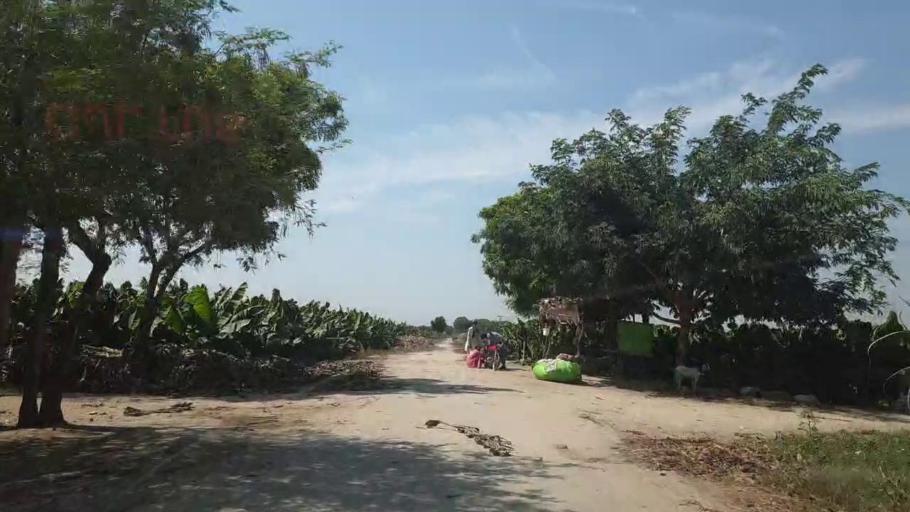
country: PK
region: Sindh
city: Tando Jam
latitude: 25.3990
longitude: 68.6312
